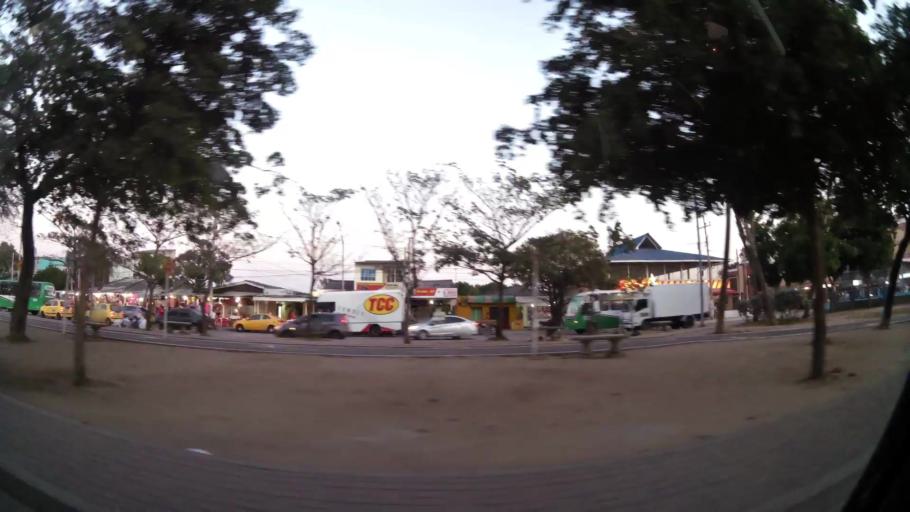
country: CO
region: Atlantico
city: Soledad
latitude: 10.9412
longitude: -74.7783
